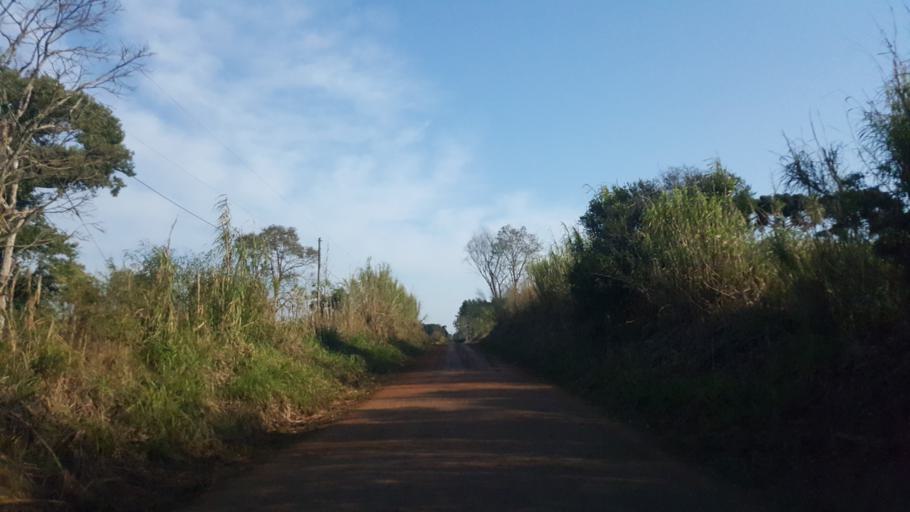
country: AR
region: Misiones
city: Capiovi
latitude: -26.9190
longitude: -55.0611
